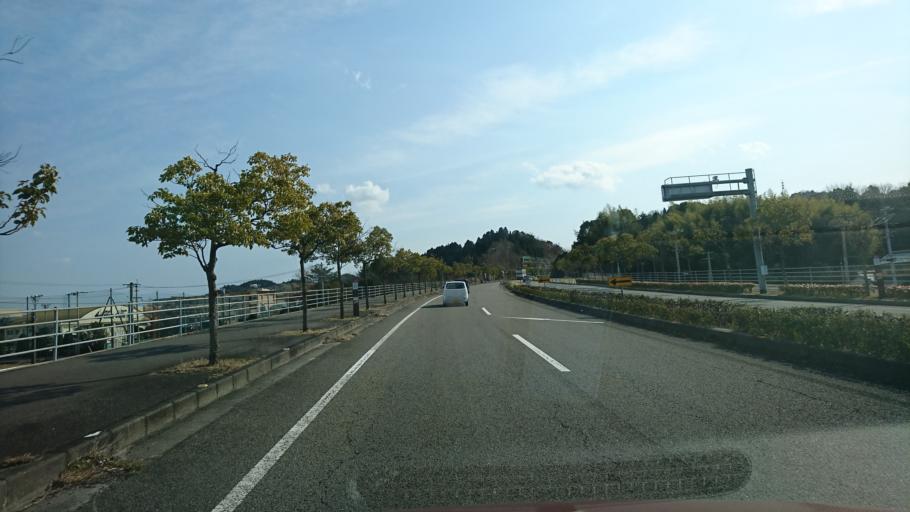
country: JP
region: Ehime
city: Saijo
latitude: 34.0176
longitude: 133.0310
